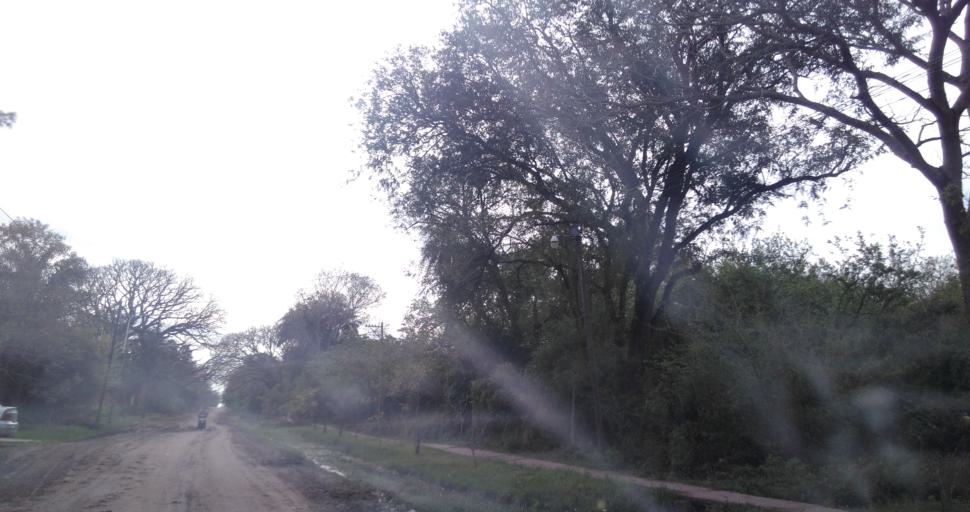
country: AR
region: Chaco
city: Colonia Benitez
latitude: -27.3322
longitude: -58.9532
